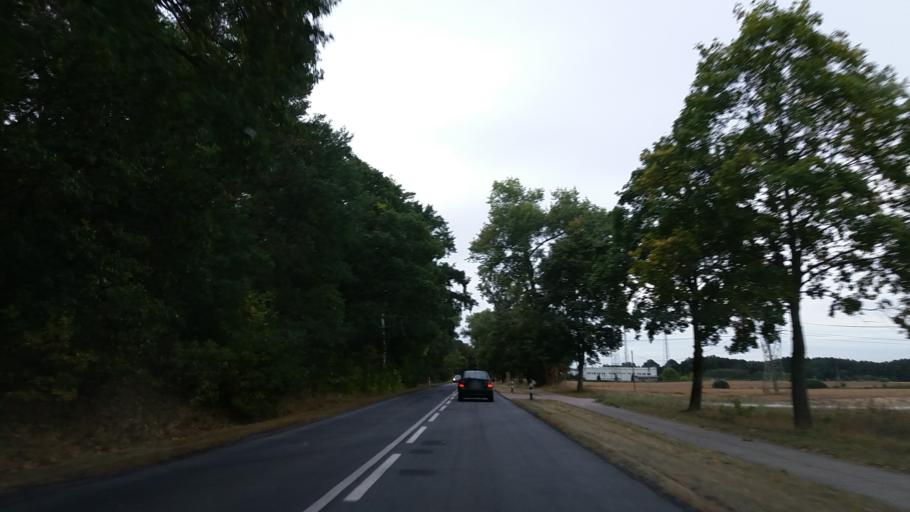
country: PL
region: Lubusz
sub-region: Powiat gorzowski
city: Klodawa
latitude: 52.7988
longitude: 15.2183
